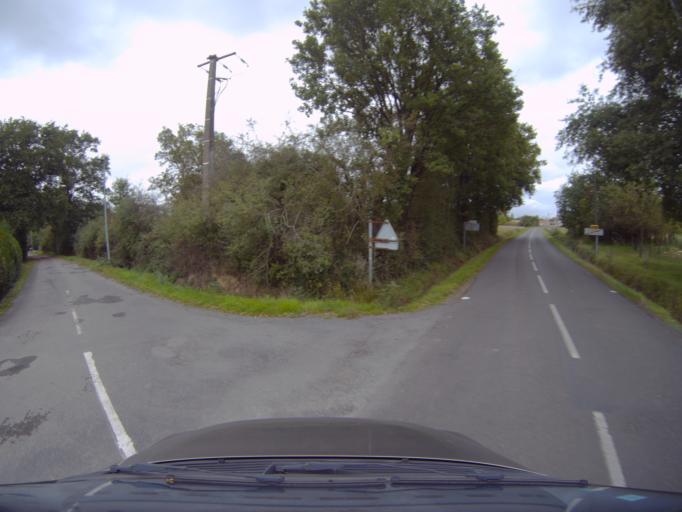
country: FR
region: Pays de la Loire
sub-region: Departement de la Loire-Atlantique
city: Clisson
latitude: 47.1043
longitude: -1.2655
